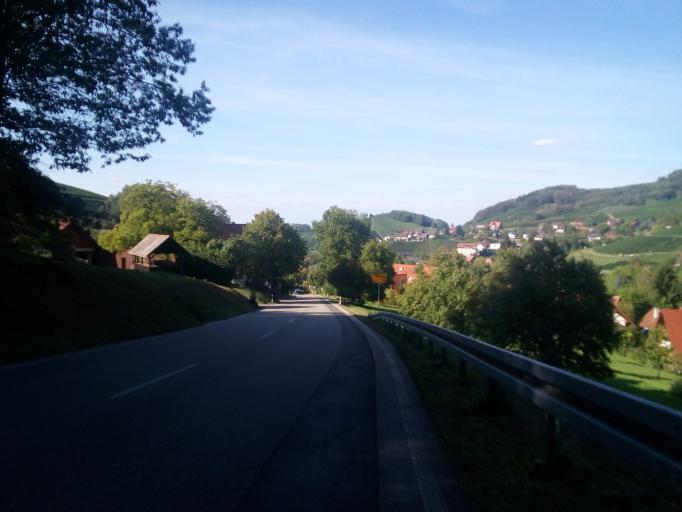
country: DE
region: Baden-Wuerttemberg
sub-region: Freiburg Region
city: Sasbachwalden
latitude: 48.6116
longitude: 8.1306
